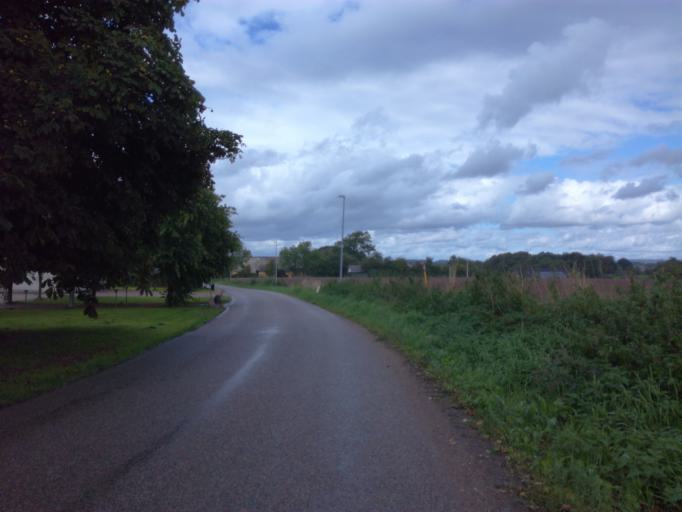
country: DK
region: South Denmark
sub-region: Fredericia Kommune
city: Fredericia
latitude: 55.6062
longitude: 9.7239
